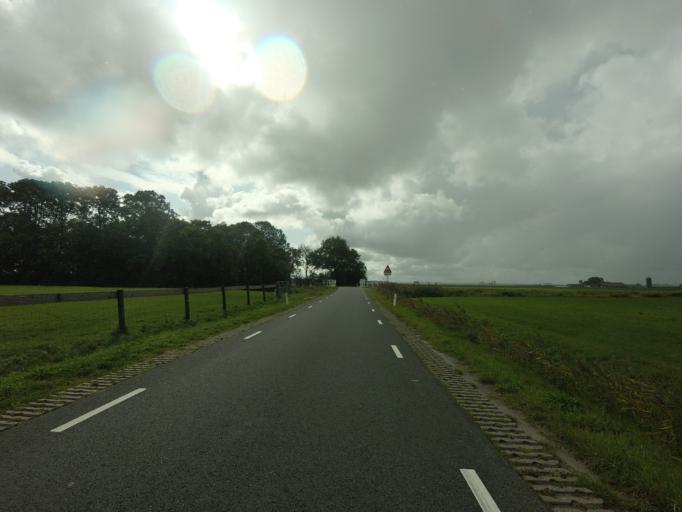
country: NL
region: Friesland
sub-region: Gemeente Boarnsterhim
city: Wergea
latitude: 53.1487
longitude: 5.8344
